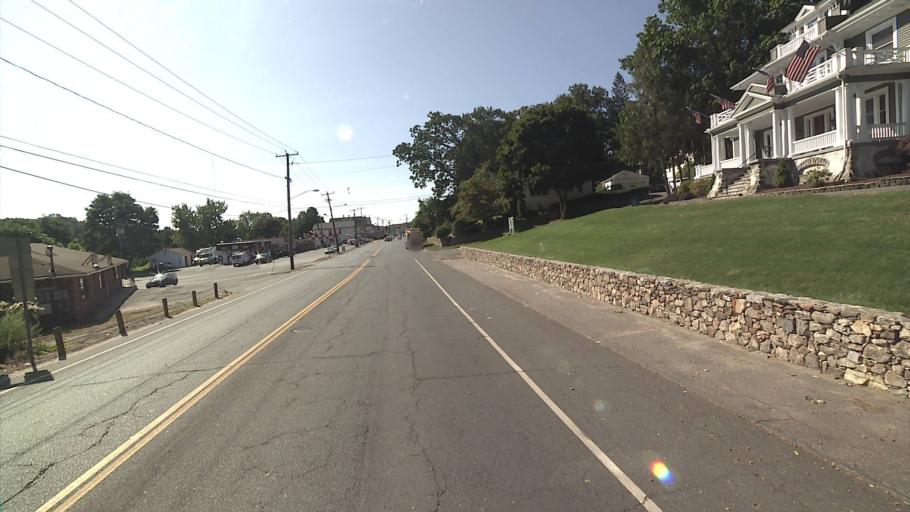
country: US
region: Connecticut
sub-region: New Haven County
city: Waterbury
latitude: 41.5717
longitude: -73.0621
